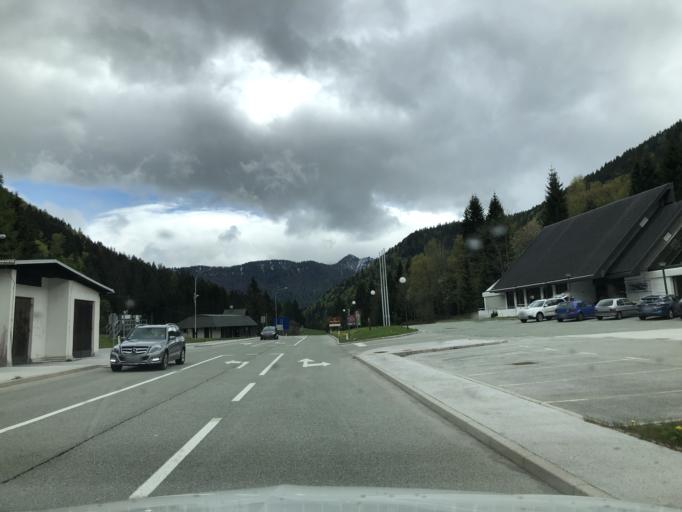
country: AT
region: Carinthia
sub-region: Politischer Bezirk Villach Land
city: Arnoldstein
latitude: 46.5174
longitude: 13.7515
